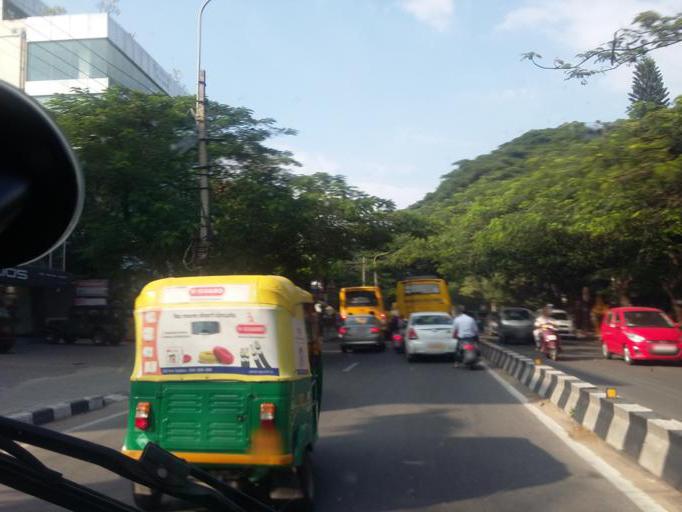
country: IN
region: Karnataka
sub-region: Bangalore Urban
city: Bangalore
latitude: 12.9680
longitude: 77.6414
